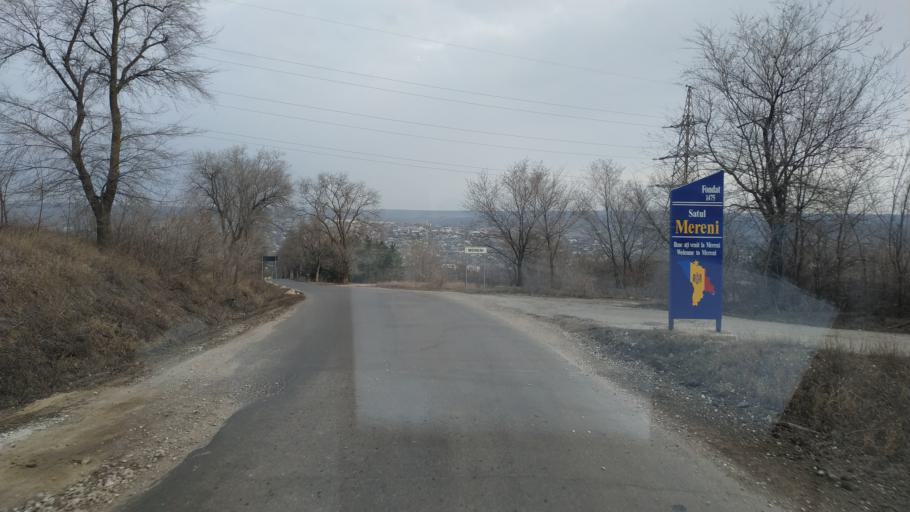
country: MD
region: Chisinau
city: Singera
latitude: 46.9507
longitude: 29.0574
